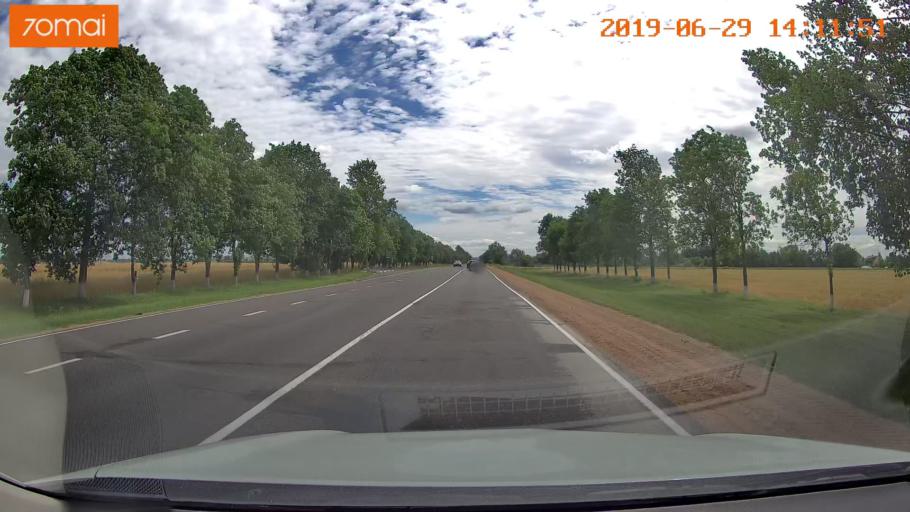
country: BY
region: Minsk
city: Salihorsk
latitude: 52.8153
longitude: 27.5052
